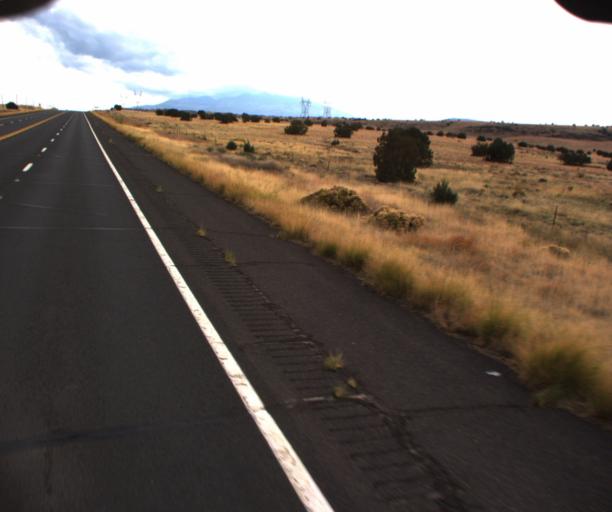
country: US
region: Arizona
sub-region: Coconino County
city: Flagstaff
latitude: 35.5469
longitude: -111.5377
